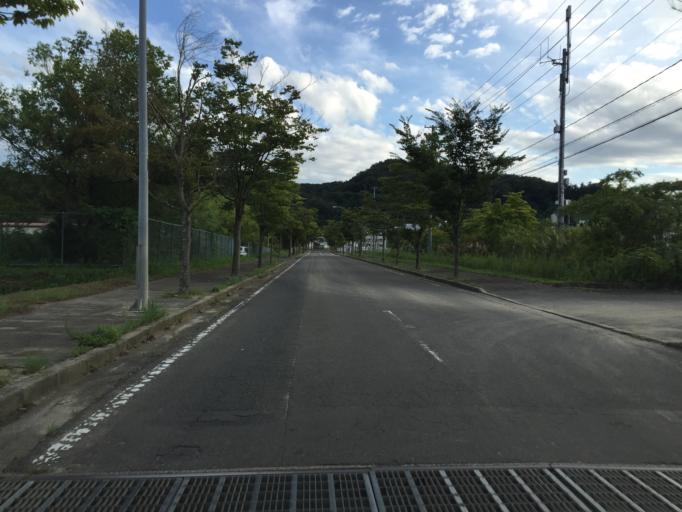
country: JP
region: Fukushima
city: Hobaramachi
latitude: 37.7894
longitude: 140.5198
